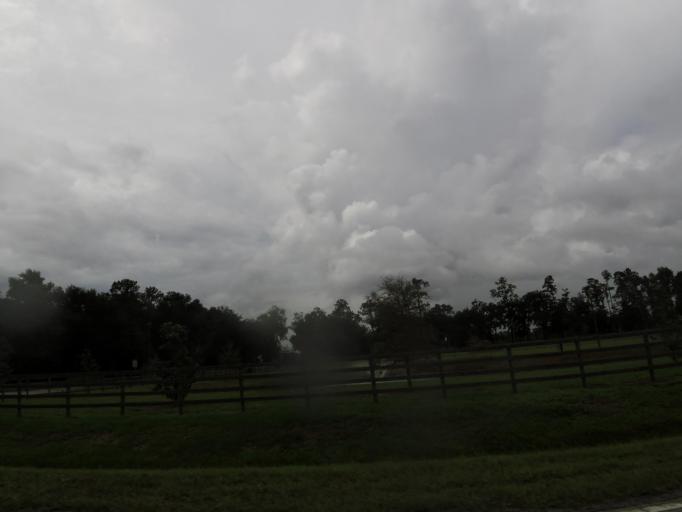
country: US
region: Florida
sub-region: Saint Johns County
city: Saint Augustine South
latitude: 29.8513
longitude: -81.5102
